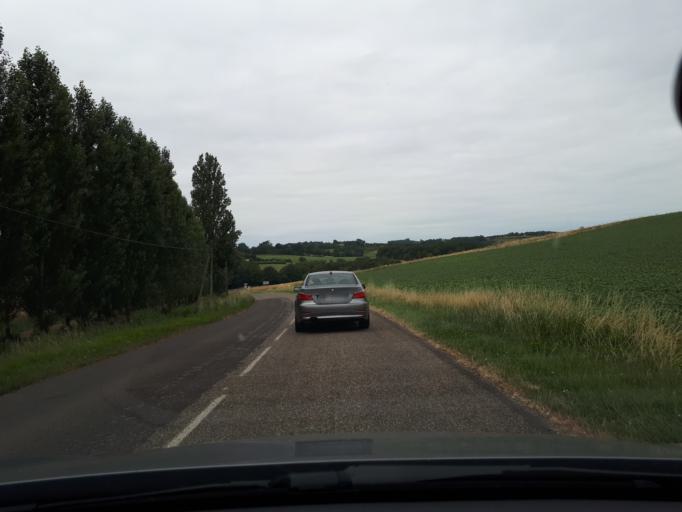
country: FR
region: Midi-Pyrenees
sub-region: Departement du Gers
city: Lectoure
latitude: 43.9332
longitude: 0.5453
